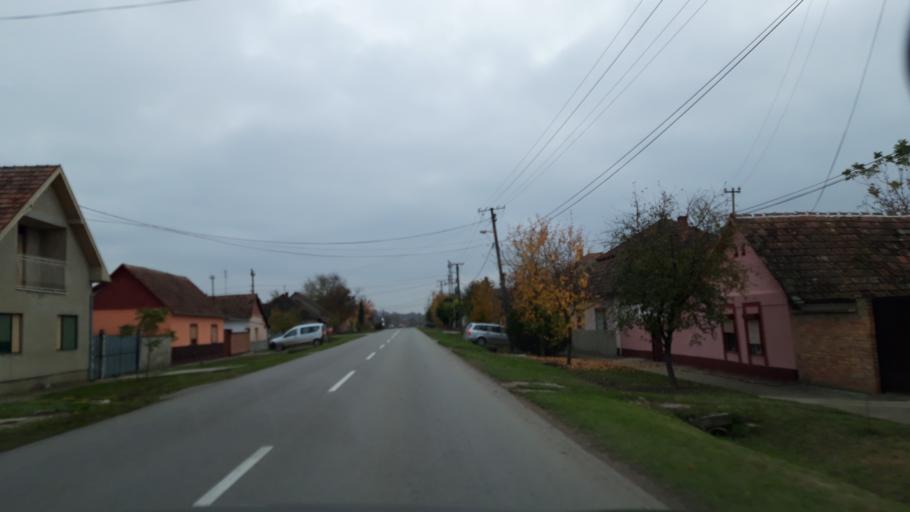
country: RS
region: Autonomna Pokrajina Vojvodina
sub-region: Severnobanatski Okrug
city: Novi Knezevac
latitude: 46.0565
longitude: 20.1001
